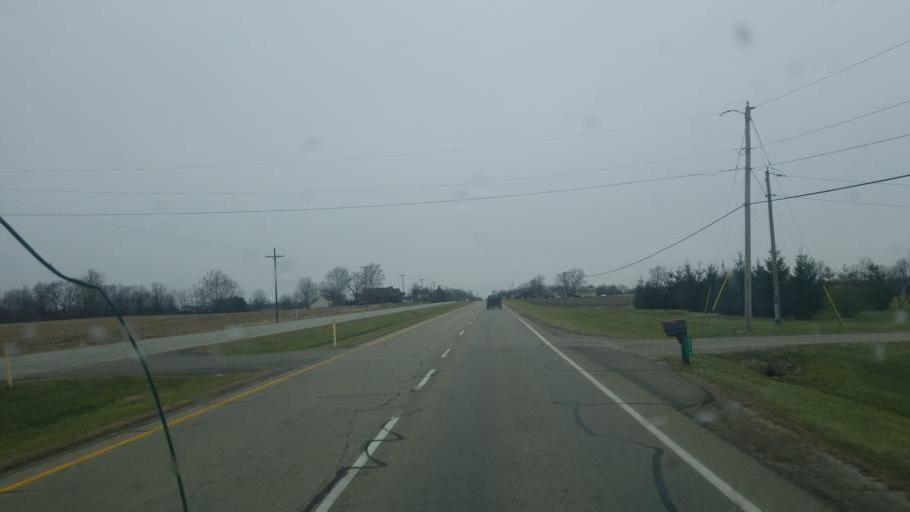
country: US
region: Indiana
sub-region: Henry County
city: Knightstown
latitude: 39.7910
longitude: -85.6307
